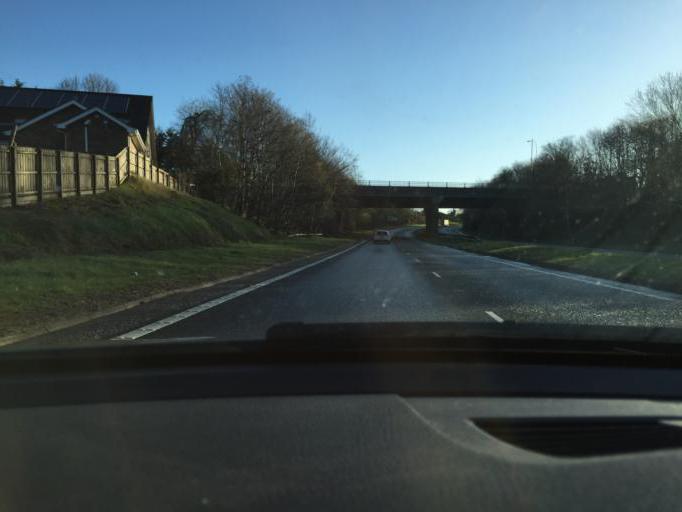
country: GB
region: Northern Ireland
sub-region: Banbridge District
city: Banbridge
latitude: 54.3436
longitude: -6.2558
